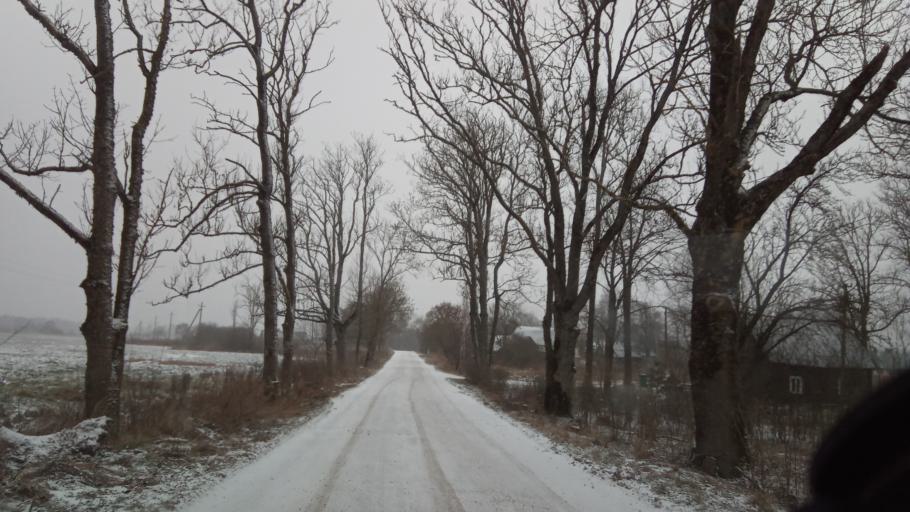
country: LT
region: Vilnius County
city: Ukmerge
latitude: 55.3168
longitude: 24.9617
